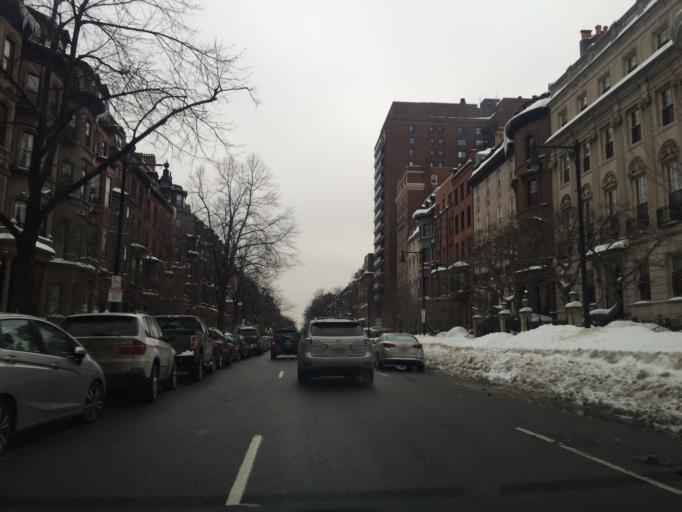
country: US
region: Massachusetts
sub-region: Suffolk County
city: Boston
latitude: 42.3547
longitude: -71.0752
